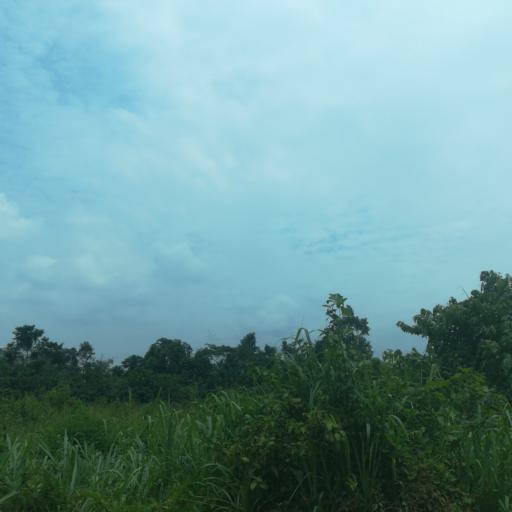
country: NG
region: Lagos
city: Ejirin
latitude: 6.6812
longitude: 3.7992
